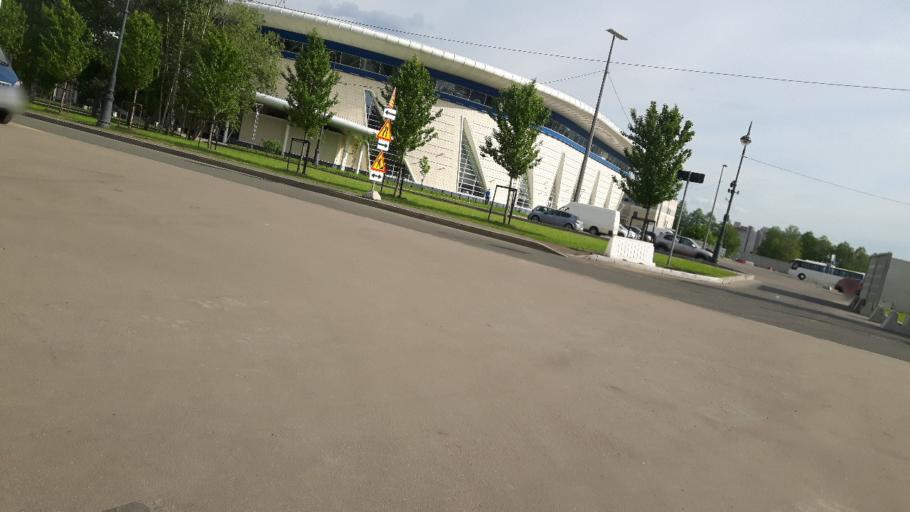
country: RU
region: St.-Petersburg
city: Staraya Derevnya
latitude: 59.9723
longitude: 30.2291
